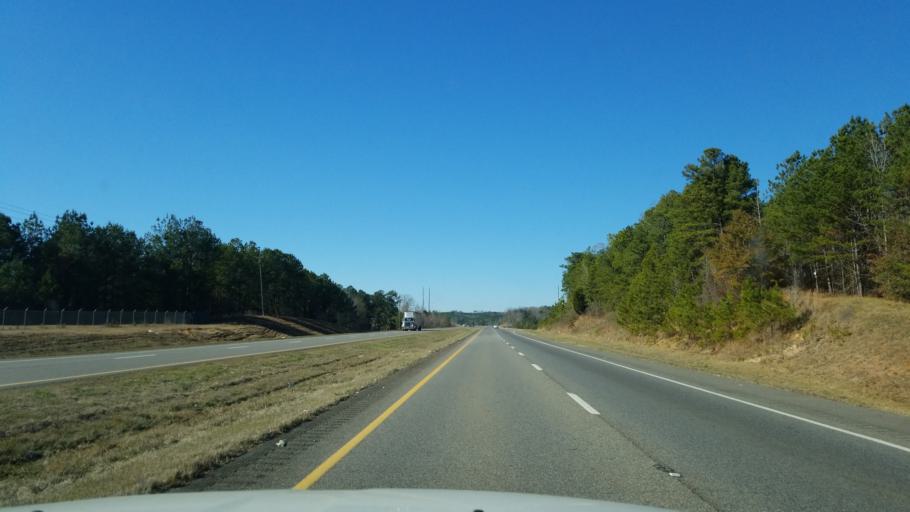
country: US
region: Alabama
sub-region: Tuscaloosa County
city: Northport
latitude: 33.2590
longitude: -87.7000
